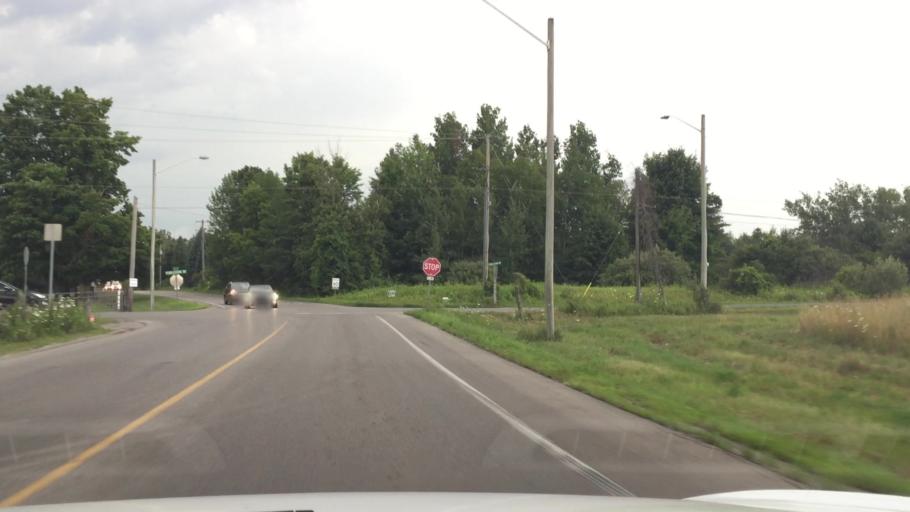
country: CA
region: Ontario
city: Oshawa
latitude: 43.9317
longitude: -78.7977
